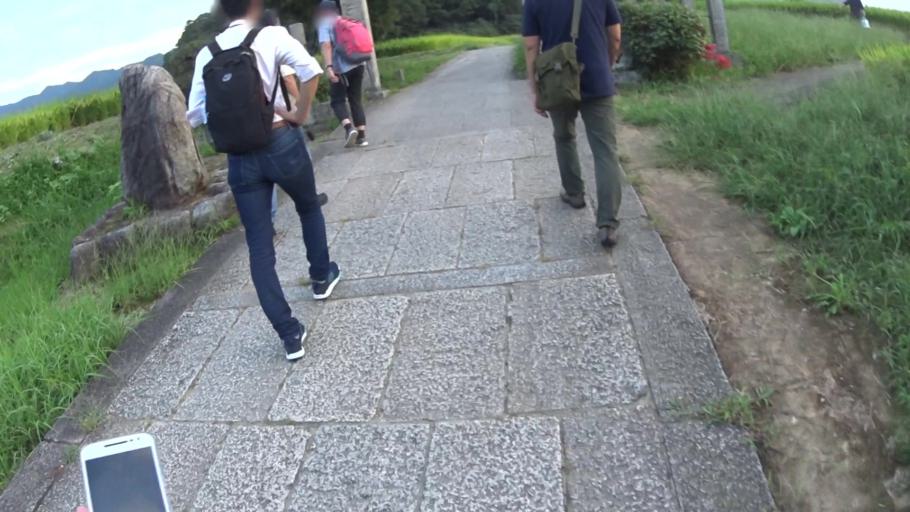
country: JP
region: Nara
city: Kashihara-shi
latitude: 34.4709
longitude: 135.8160
